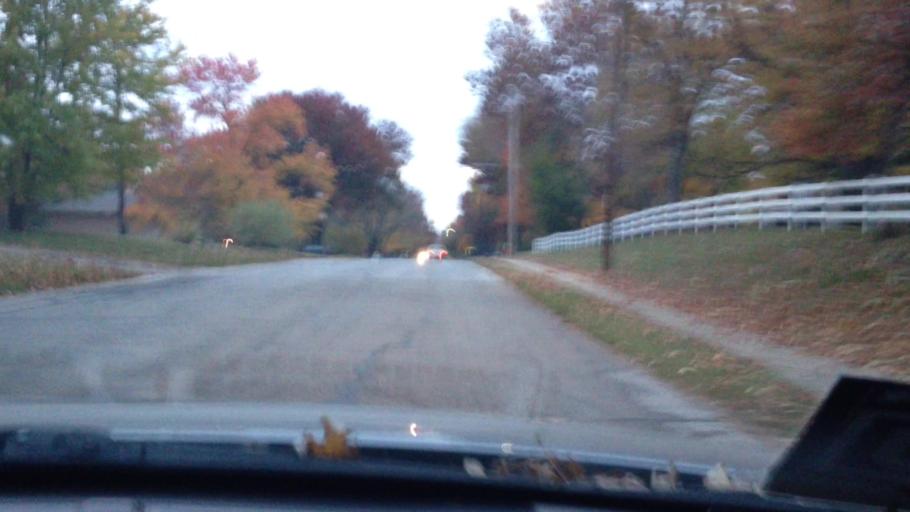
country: US
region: Kansas
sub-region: Leavenworth County
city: Leavenworth
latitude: 39.2906
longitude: -94.9340
